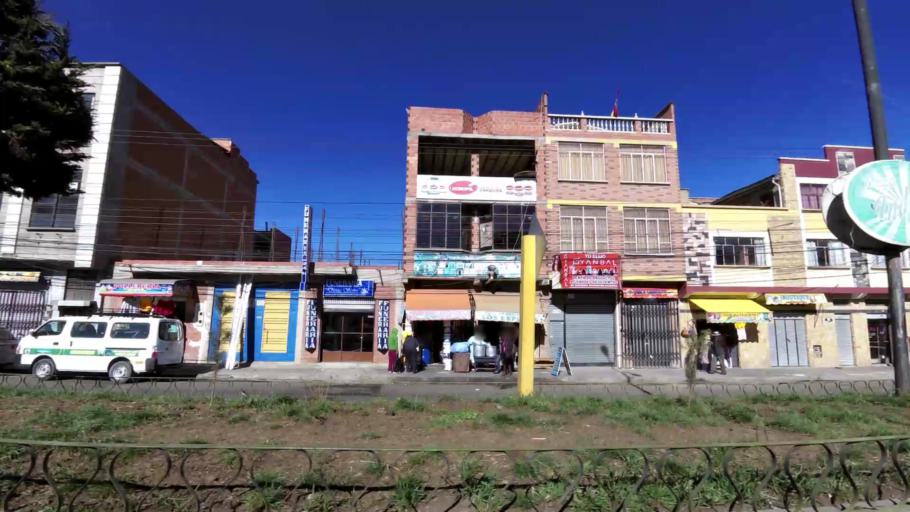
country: BO
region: La Paz
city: La Paz
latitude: -16.5324
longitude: -68.1933
